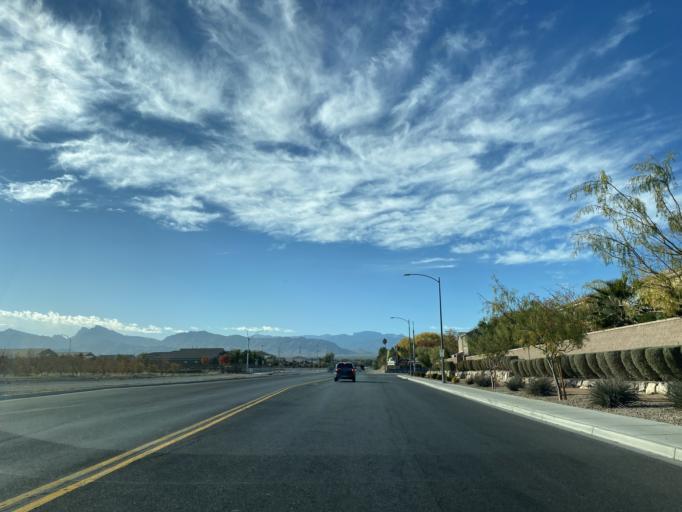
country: US
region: Nevada
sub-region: Clark County
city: North Las Vegas
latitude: 36.3052
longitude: -115.2497
